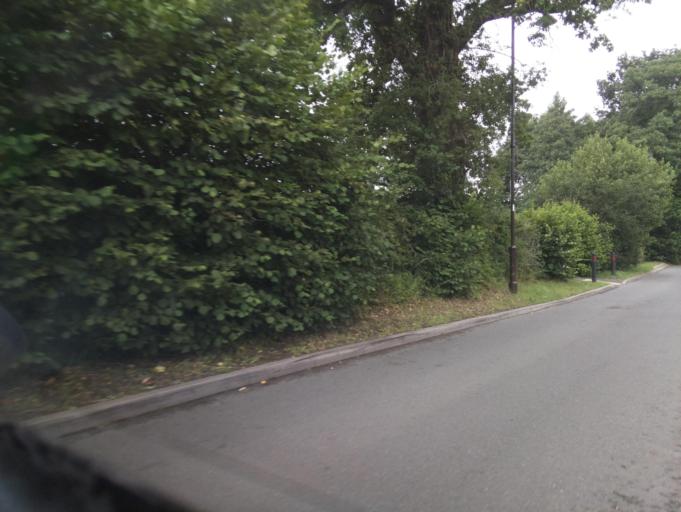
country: GB
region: England
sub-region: Solihull
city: Dickens Heath
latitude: 52.3820
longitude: -1.8411
